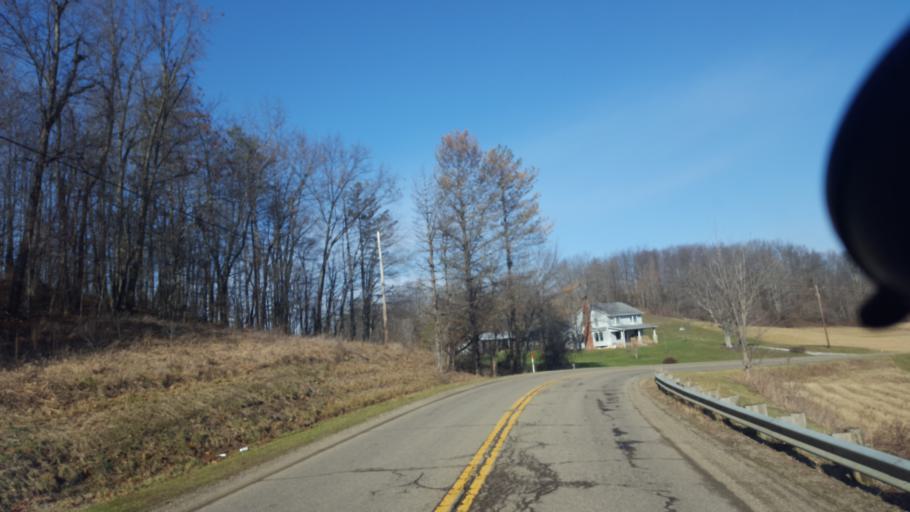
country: US
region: Ohio
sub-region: Tuscarawas County
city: Newcomerstown
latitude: 40.1923
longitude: -81.5268
